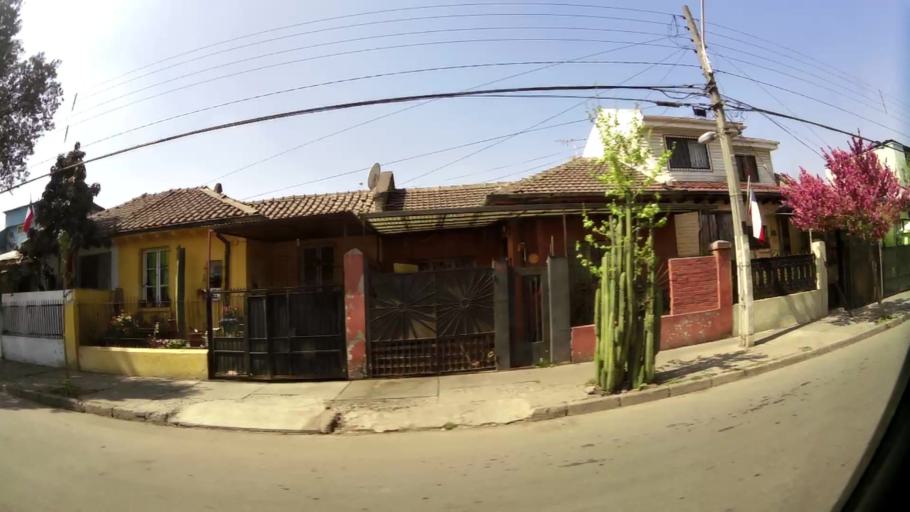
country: CL
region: Santiago Metropolitan
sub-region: Provincia de Santiago
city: Santiago
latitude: -33.4715
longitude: -70.6729
